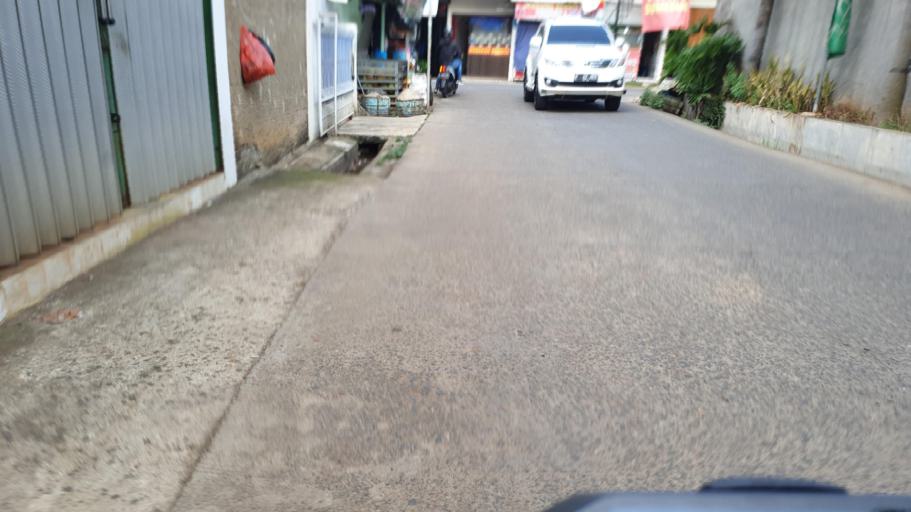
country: ID
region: West Java
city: Depok
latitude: -6.3665
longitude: 106.8498
